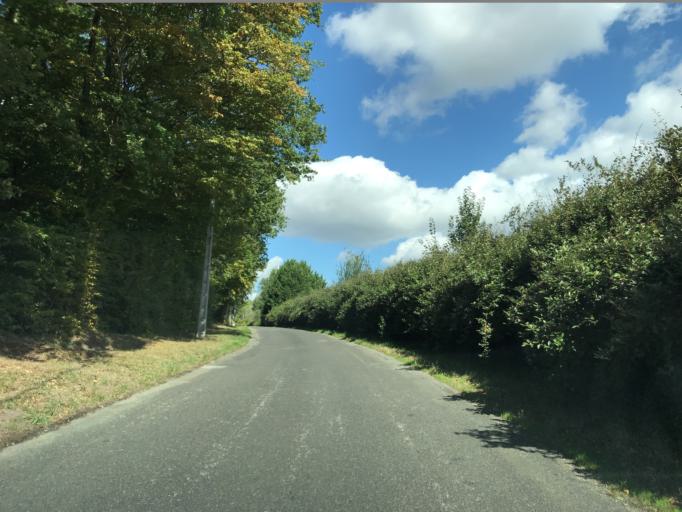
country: FR
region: Haute-Normandie
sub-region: Departement de l'Eure
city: La Chapelle-Reanville
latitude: 49.0880
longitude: 1.3963
